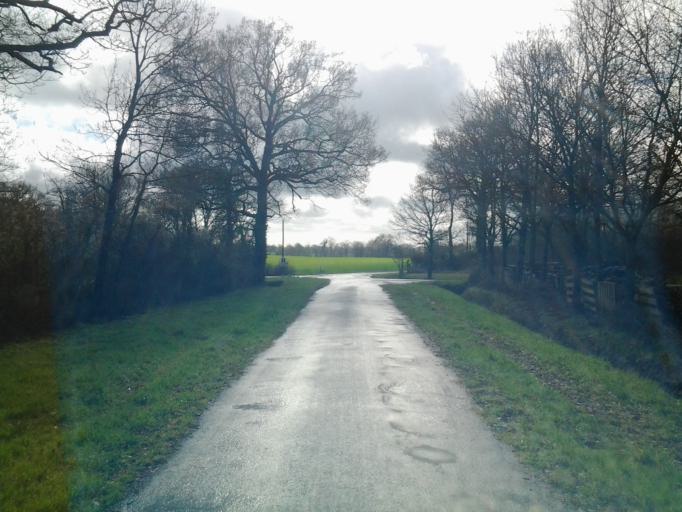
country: FR
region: Pays de la Loire
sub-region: Departement de la Vendee
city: La Chaize-le-Vicomte
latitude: 46.6570
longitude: -1.3505
